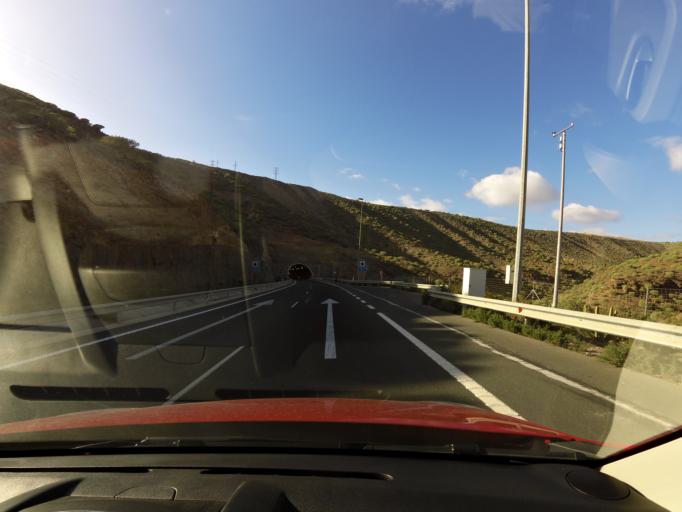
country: ES
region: Canary Islands
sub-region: Provincia de Las Palmas
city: Puerto Rico
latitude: 27.7837
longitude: -15.6799
